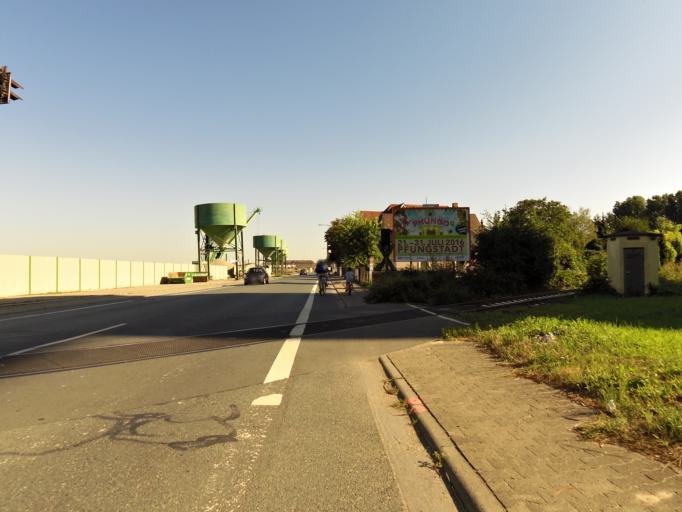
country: DE
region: Hesse
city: Gernsheim
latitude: 49.7581
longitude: 8.4829
